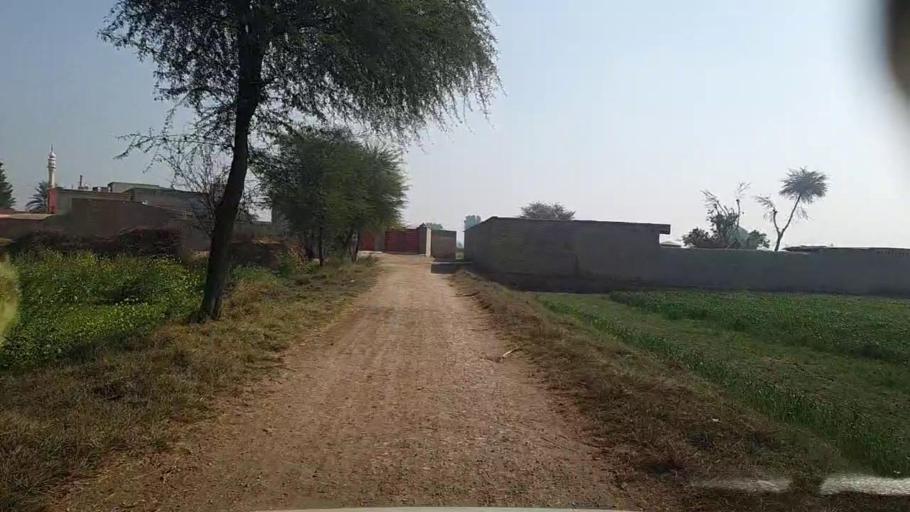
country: PK
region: Sindh
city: Khairpur
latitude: 27.9421
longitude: 69.6767
